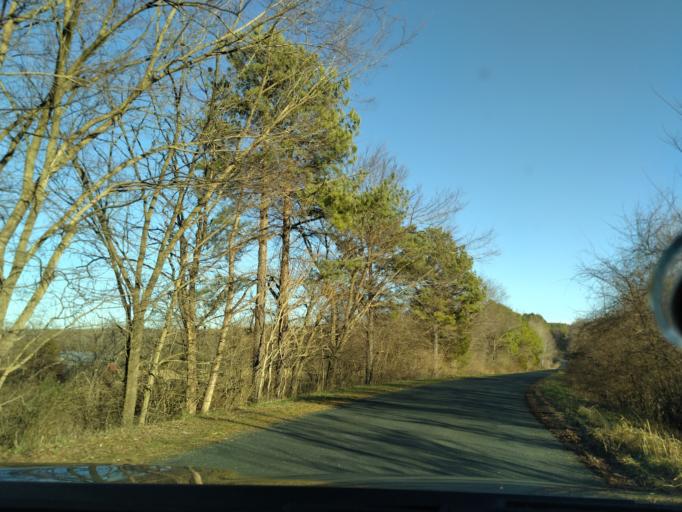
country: US
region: Virginia
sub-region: Appomattox County
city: Appomattox
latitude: 37.3751
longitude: -78.6393
